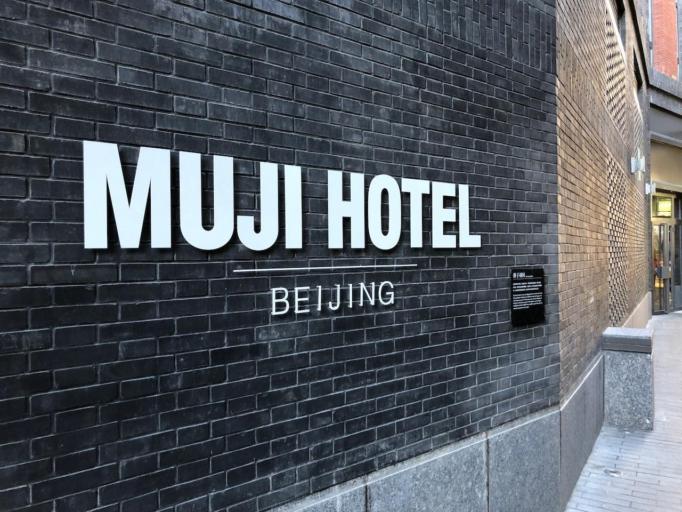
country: CN
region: Beijing
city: Beijing
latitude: 39.8971
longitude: 116.3894
